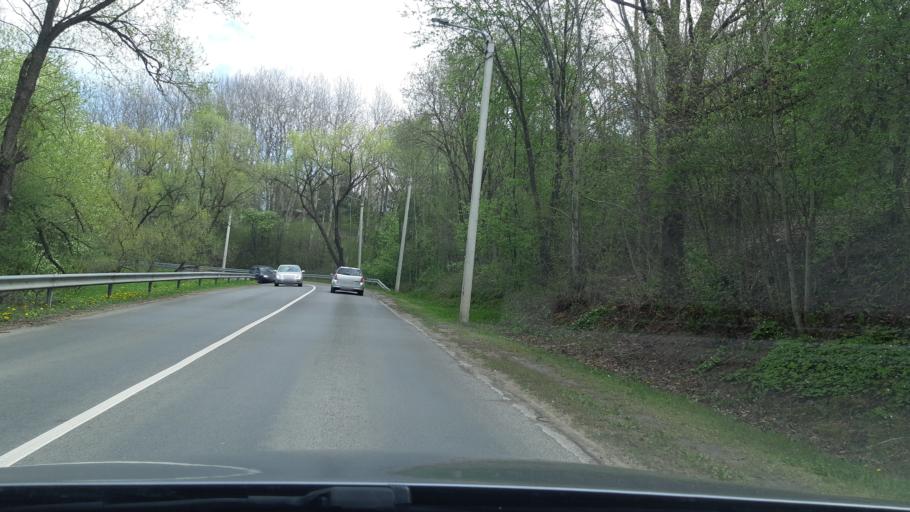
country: LT
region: Kauno apskritis
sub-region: Kaunas
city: Silainiai
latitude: 54.9225
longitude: 23.8632
